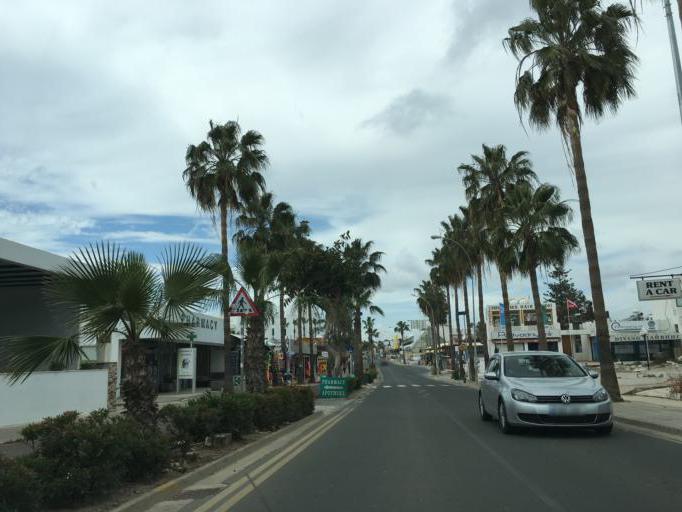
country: CY
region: Ammochostos
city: Ayia Napa
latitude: 34.9864
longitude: 34.0078
